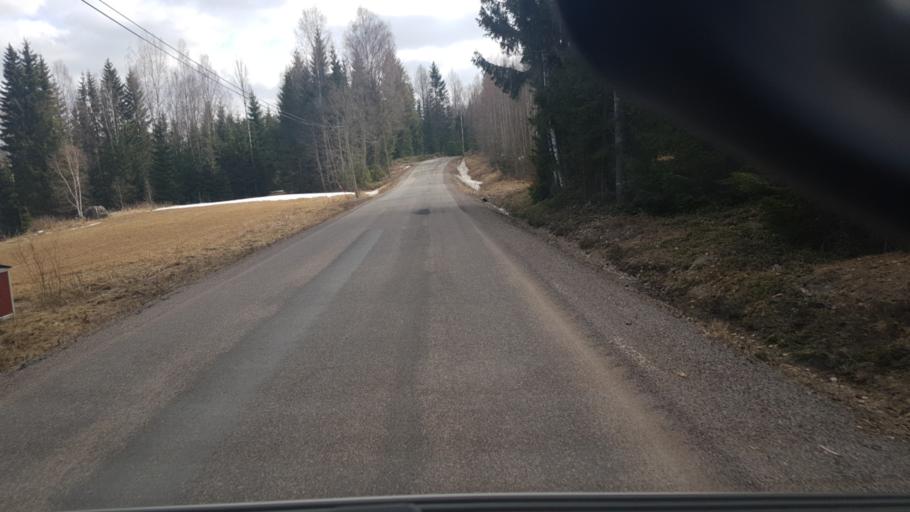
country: SE
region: Vaermland
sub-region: Eda Kommun
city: Amotfors
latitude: 59.8666
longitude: 12.4274
